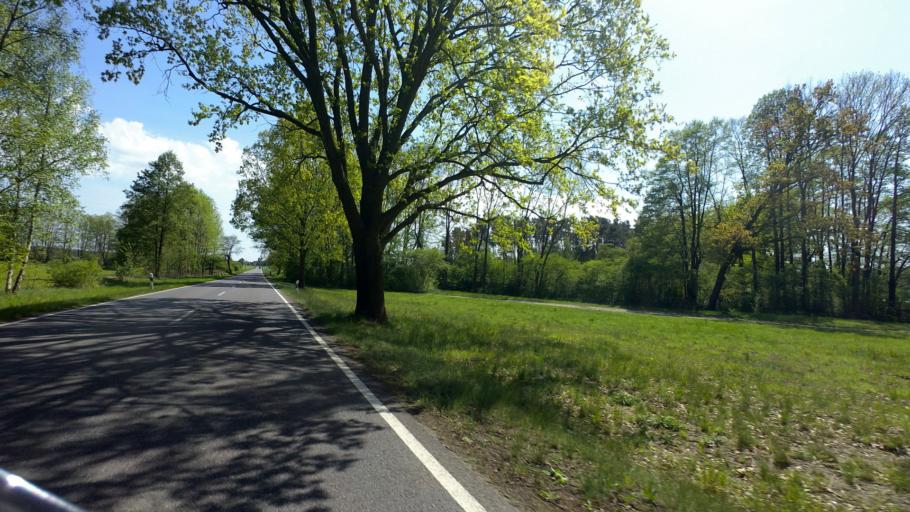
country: DE
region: Brandenburg
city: Lieberose
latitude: 51.9894
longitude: 14.2084
